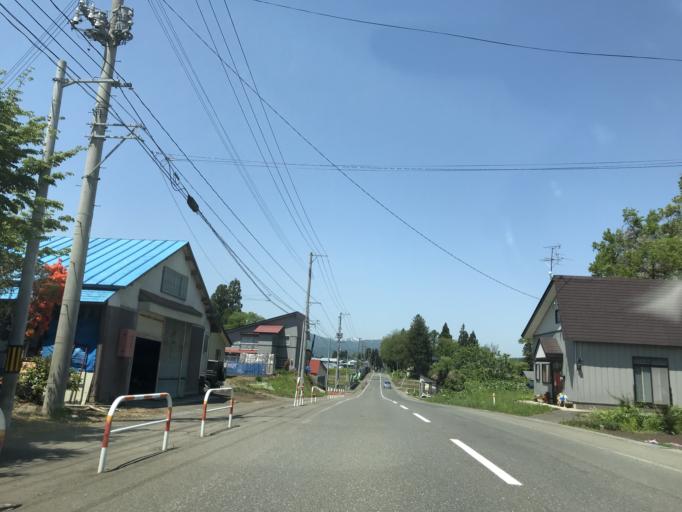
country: JP
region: Akita
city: Yokotemachi
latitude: 39.3858
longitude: 140.7582
